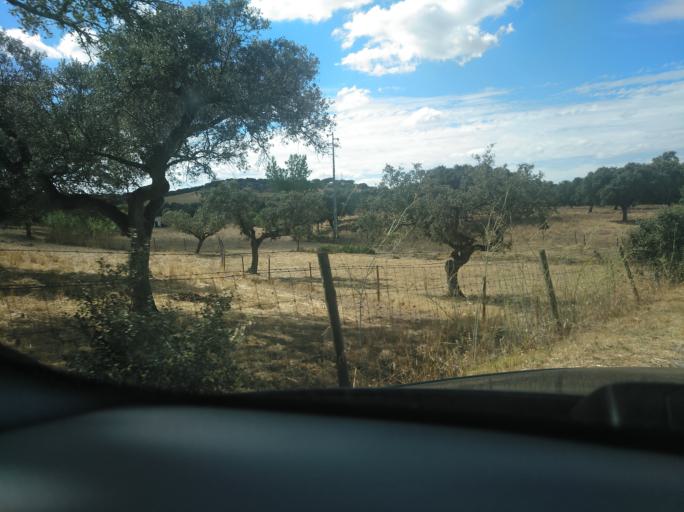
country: ES
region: Extremadura
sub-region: Provincia de Badajoz
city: La Codosera
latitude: 39.1130
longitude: -7.1500
